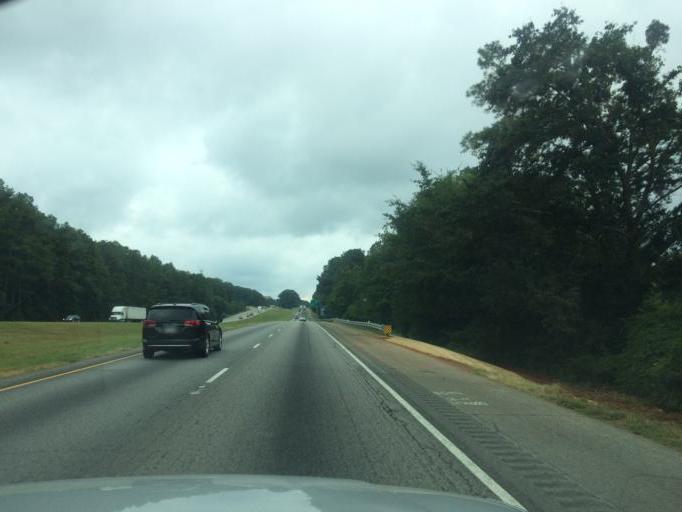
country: US
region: Georgia
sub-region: Franklin County
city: Carnesville
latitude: 34.3585
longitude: -83.2989
